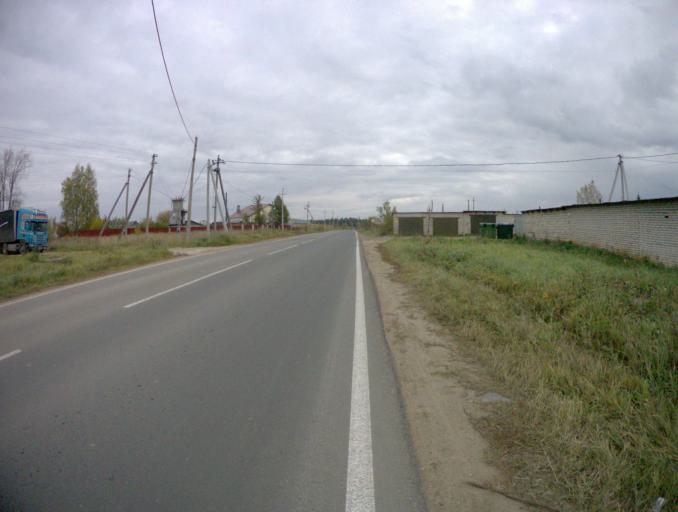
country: RU
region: Vladimir
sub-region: Kovrovskiy Rayon
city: Kovrov
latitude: 56.3712
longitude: 41.3671
